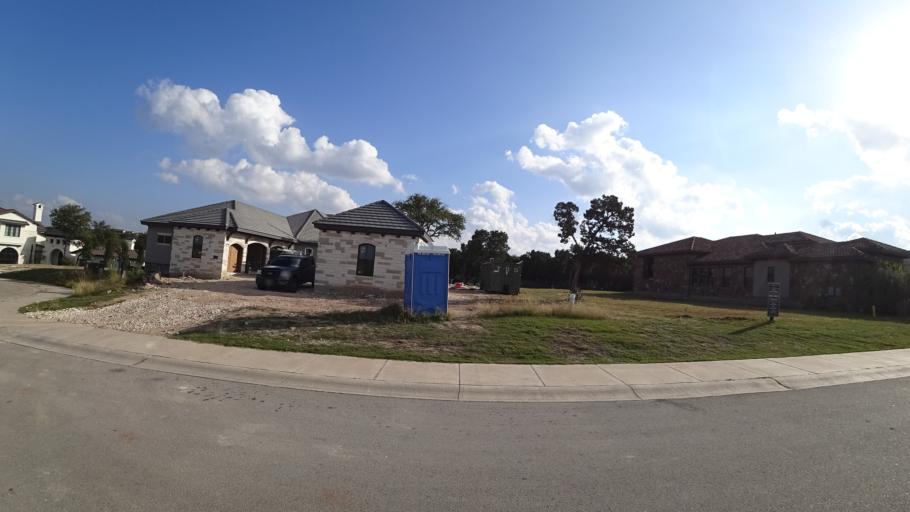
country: US
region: Texas
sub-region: Travis County
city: Barton Creek
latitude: 30.2738
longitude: -97.8740
